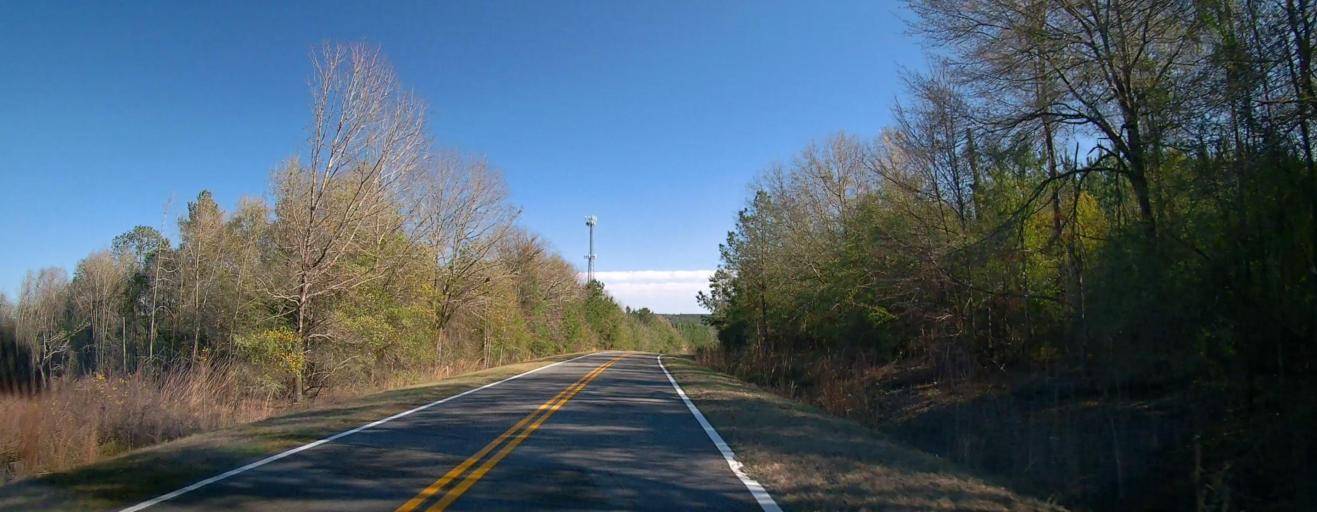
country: US
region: Georgia
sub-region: Taylor County
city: Reynolds
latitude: 32.5547
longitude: -83.9998
